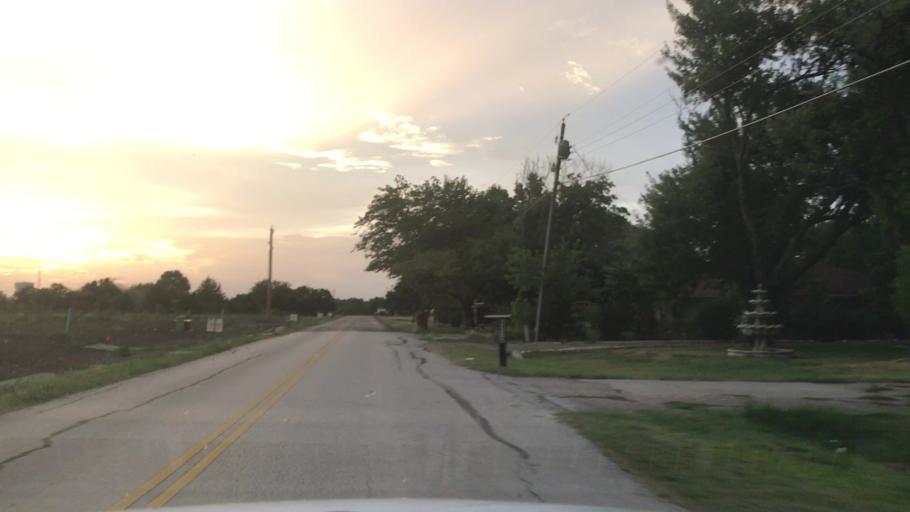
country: US
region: Texas
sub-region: Dallas County
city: Seagoville
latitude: 32.6998
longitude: -96.5524
